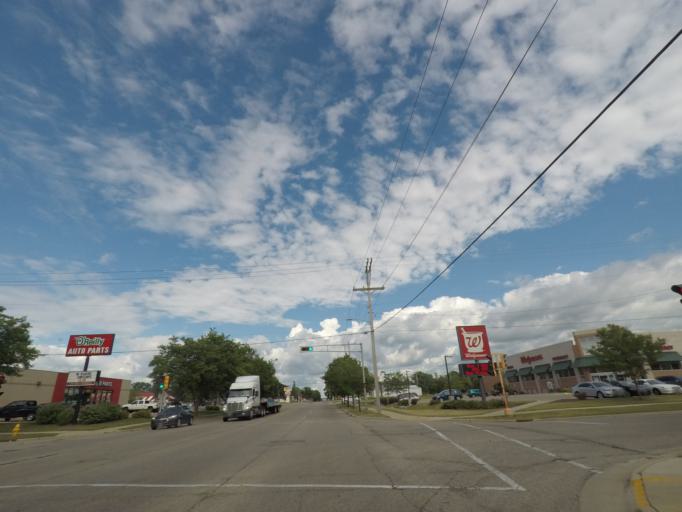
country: US
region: Wisconsin
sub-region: Rock County
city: Janesville
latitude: 42.6793
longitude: -89.0452
